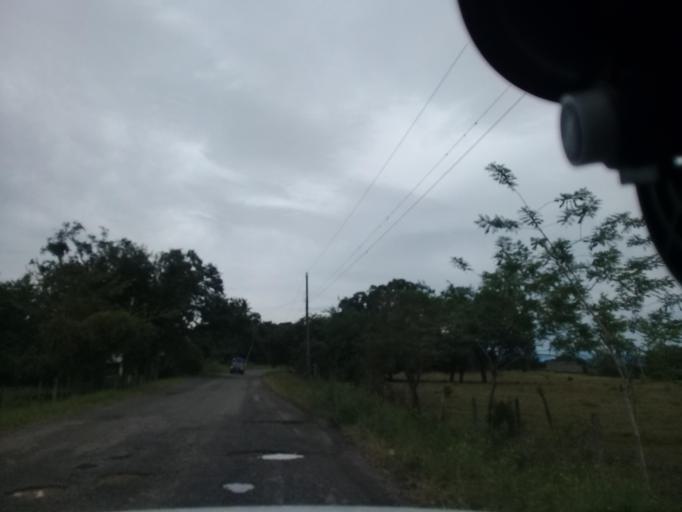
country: MX
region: Hidalgo
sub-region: Huejutla de Reyes
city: Chalahuiyapa
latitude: 21.1885
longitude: -98.3124
